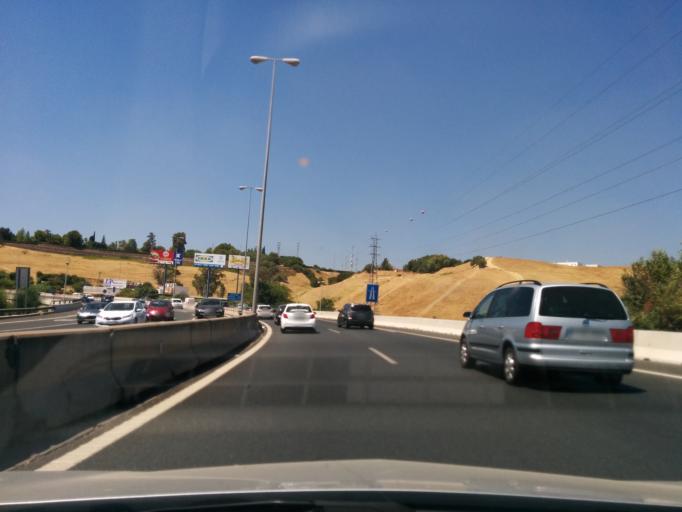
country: ES
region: Andalusia
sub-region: Provincia de Sevilla
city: Camas
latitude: 37.3899
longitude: -6.0319
